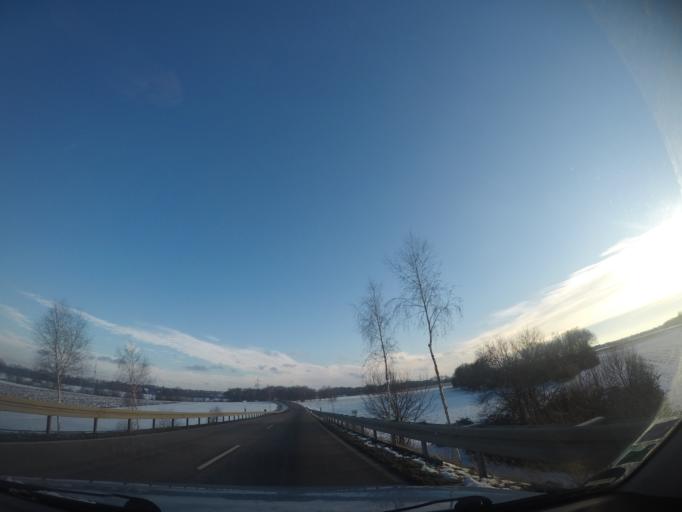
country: DE
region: Baden-Wuerttemberg
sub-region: Tuebingen Region
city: Laupheim
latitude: 48.2483
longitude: 9.8584
